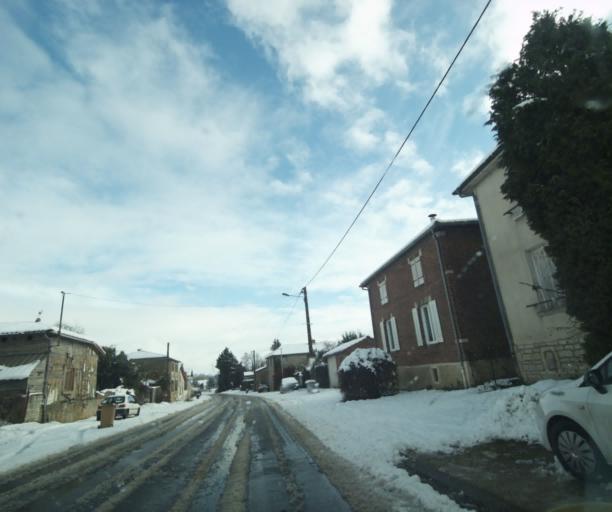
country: FR
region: Champagne-Ardenne
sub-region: Departement de la Haute-Marne
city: Montier-en-Der
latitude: 48.4548
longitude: 4.6919
